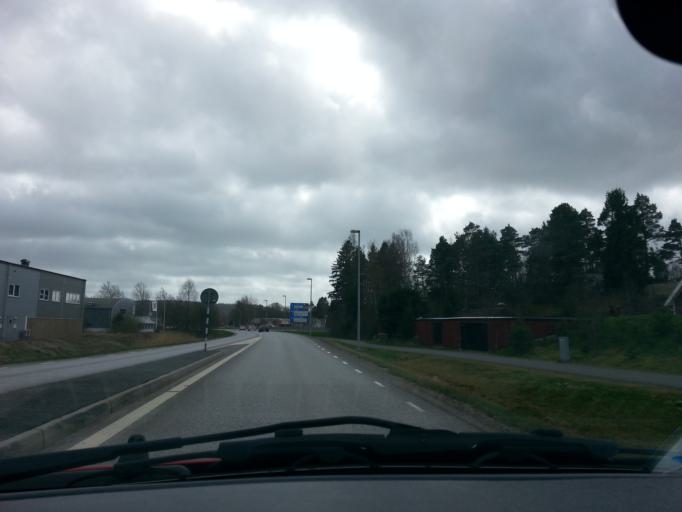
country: SE
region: Vaestra Goetaland
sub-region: Lerums Kommun
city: Stenkullen
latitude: 57.7981
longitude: 12.3078
